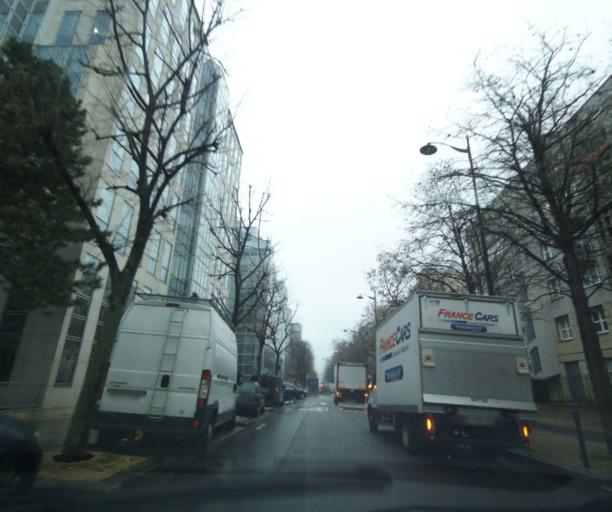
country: FR
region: Ile-de-France
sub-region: Departement des Hauts-de-Seine
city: Levallois-Perret
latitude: 48.8874
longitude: 2.2874
